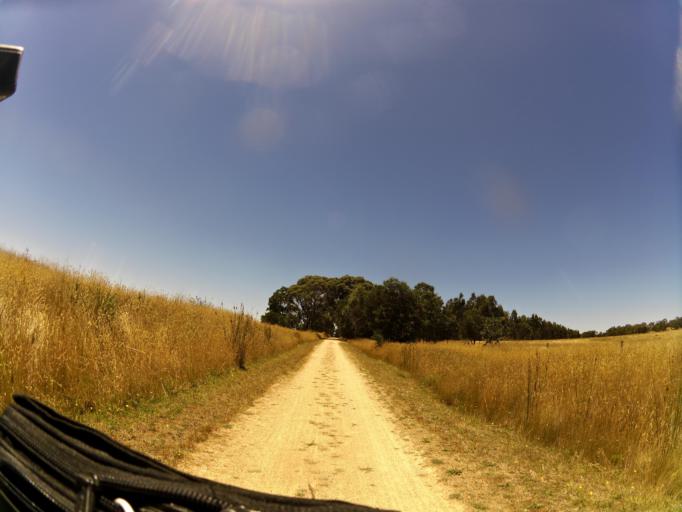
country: AU
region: Victoria
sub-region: Ballarat North
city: Delacombe
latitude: -37.5574
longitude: 143.7453
